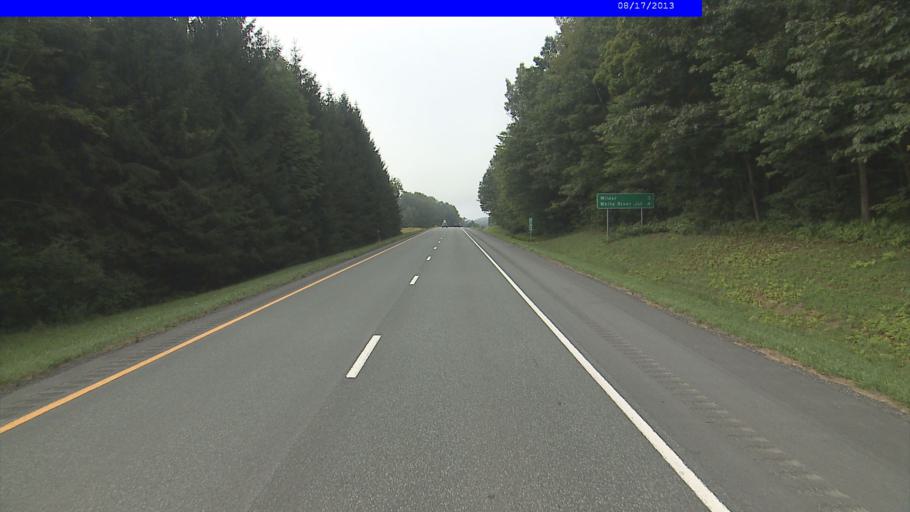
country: US
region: New Hampshire
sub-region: Grafton County
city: Hanover
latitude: 43.6976
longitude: -72.3107
